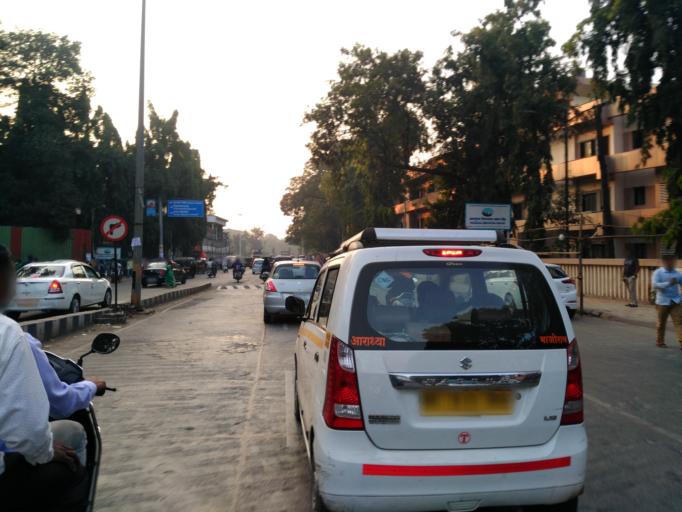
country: IN
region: Maharashtra
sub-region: Pune Division
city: Pune
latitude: 18.5011
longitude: 73.8559
